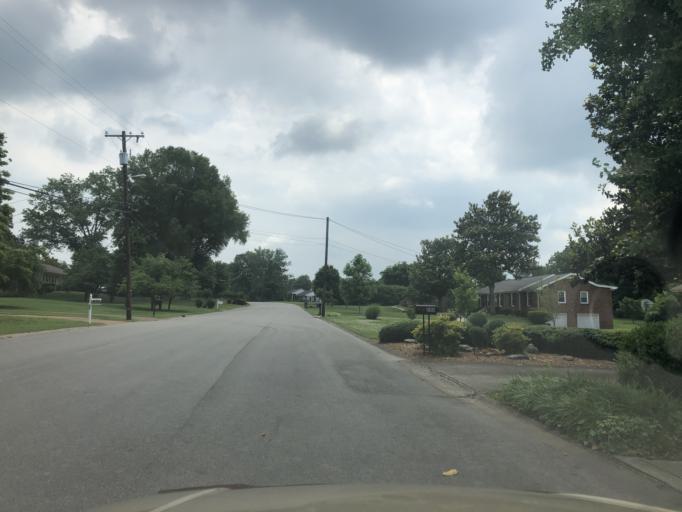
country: US
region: Tennessee
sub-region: Davidson County
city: Lakewood
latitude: 36.2356
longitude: -86.6202
